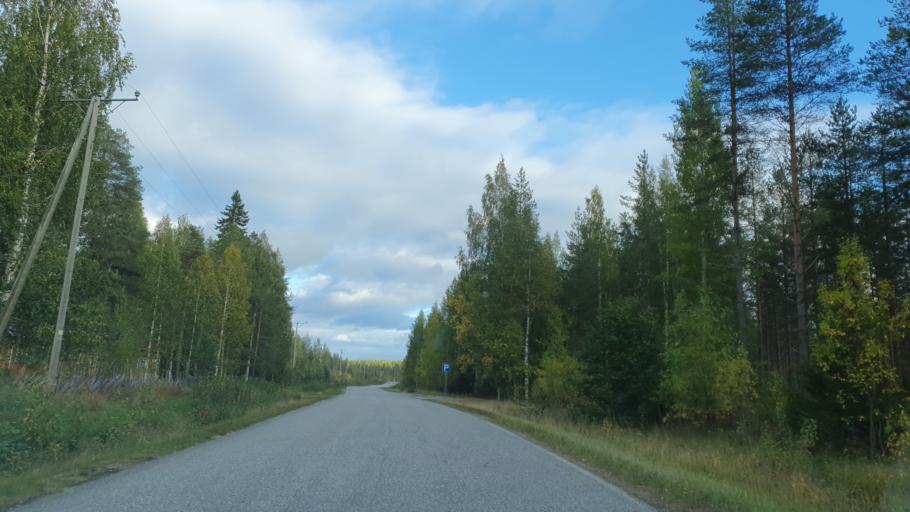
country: FI
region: Kainuu
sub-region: Kehys-Kainuu
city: Kuhmo
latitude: 63.9295
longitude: 29.9965
